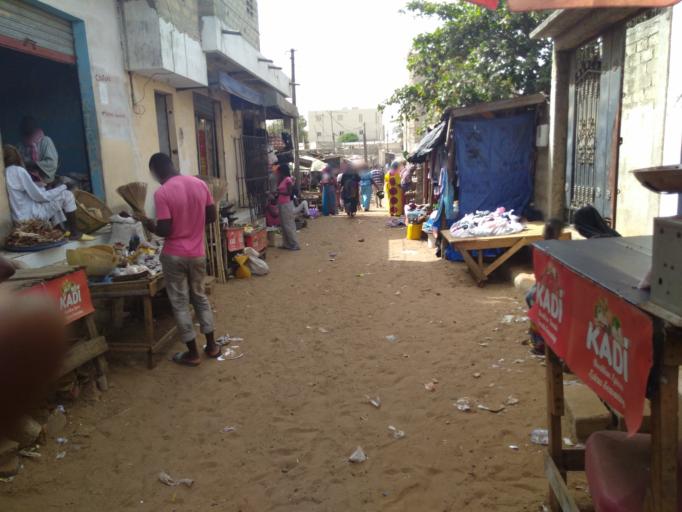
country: SN
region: Dakar
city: Pikine
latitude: 14.7933
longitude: -17.3362
